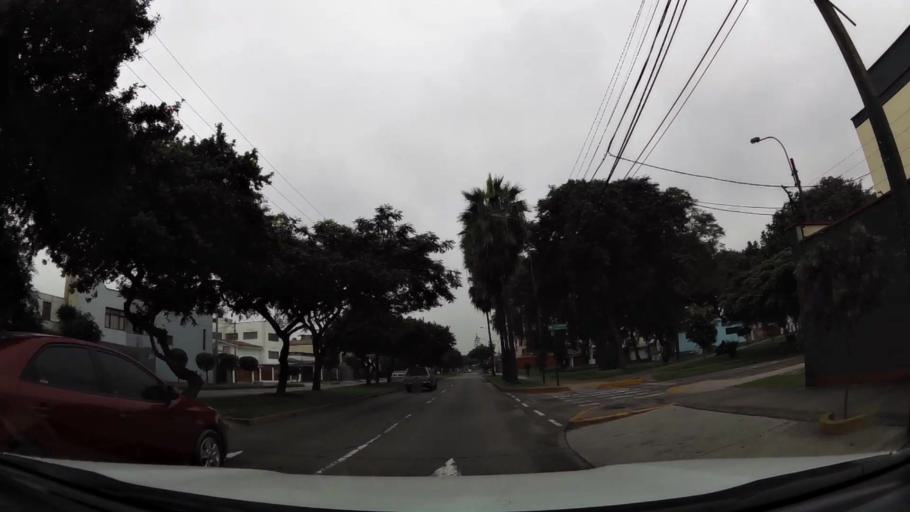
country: PE
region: Lima
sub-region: Lima
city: Surco
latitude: -12.1384
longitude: -76.9991
